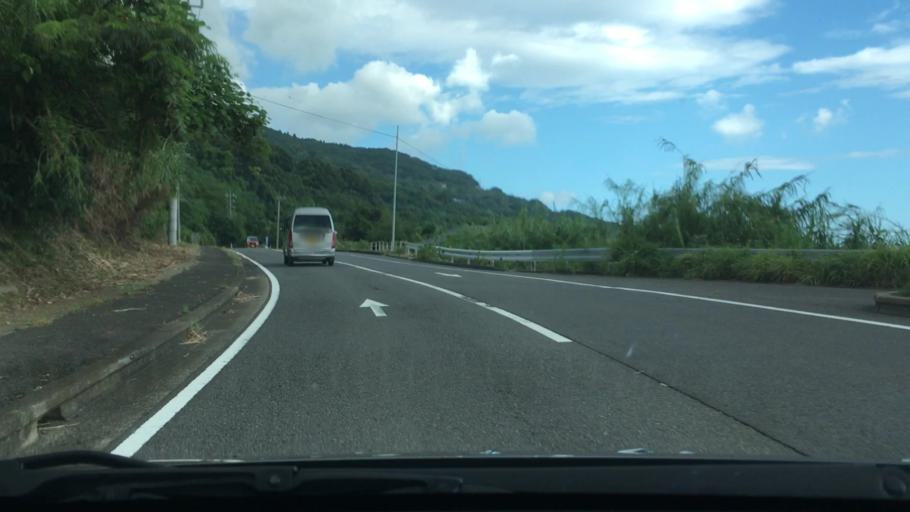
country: JP
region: Nagasaki
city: Togitsu
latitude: 32.8690
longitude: 129.6790
